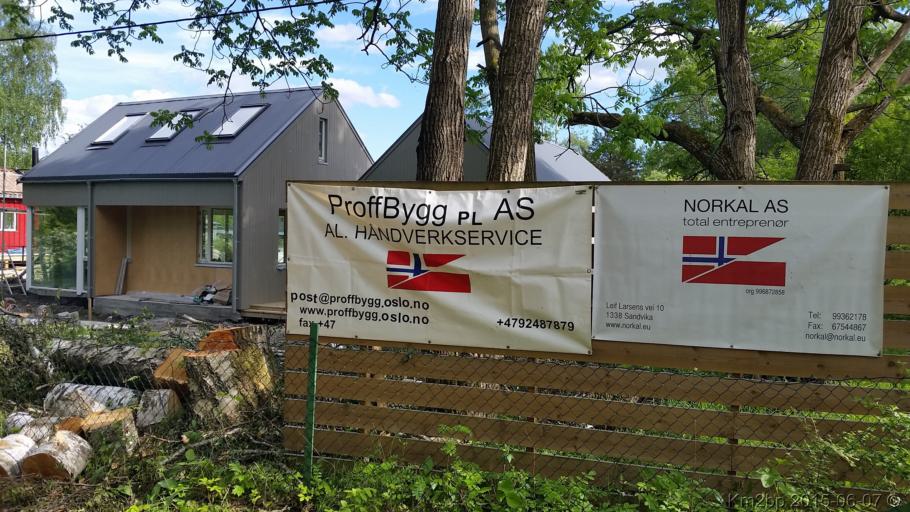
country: NO
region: Akershus
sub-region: Baerum
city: Sandvika
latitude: 59.8556
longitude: 10.5394
